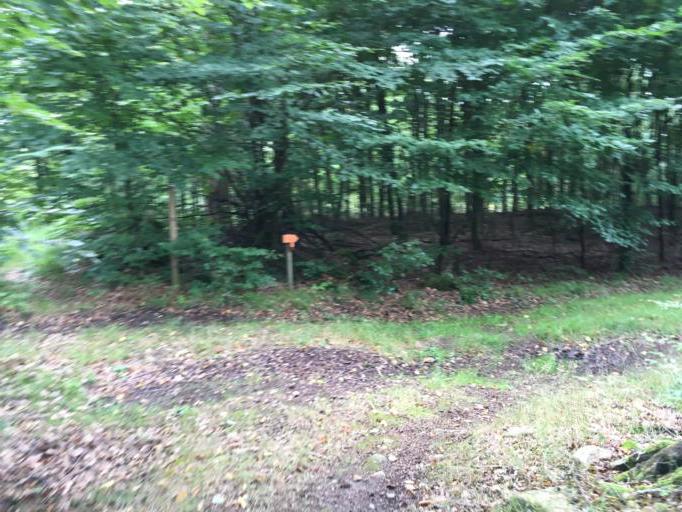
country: SE
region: Skane
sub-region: Hoors Kommun
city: Hoeoer
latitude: 55.9848
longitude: 13.4810
